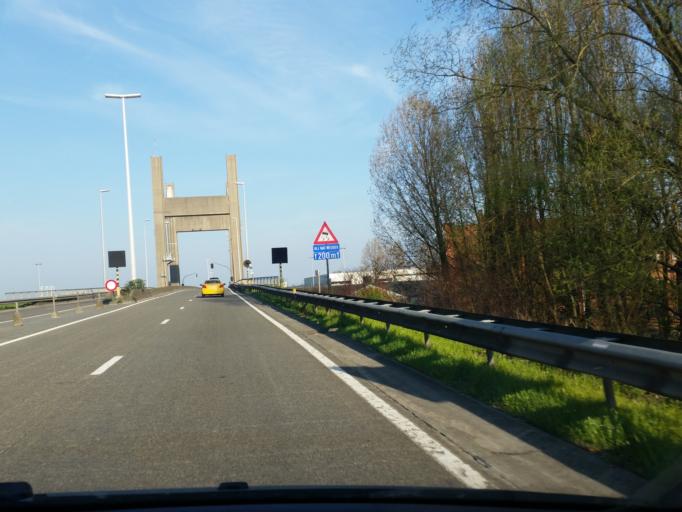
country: BE
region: Flanders
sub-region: Provincie Antwerpen
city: Willebroek
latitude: 51.0431
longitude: 4.3570
